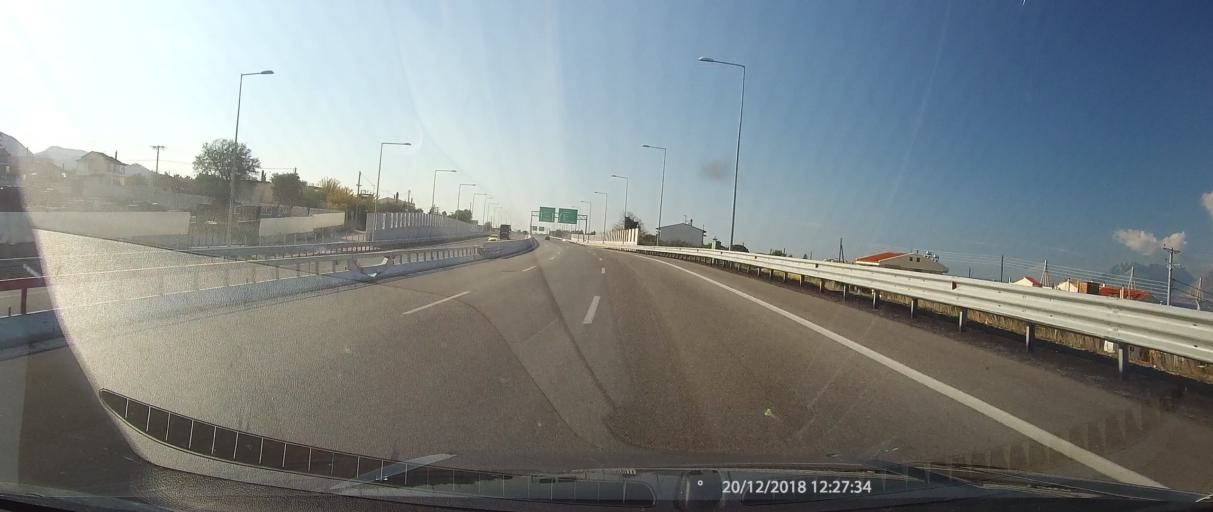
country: GR
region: West Greece
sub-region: Nomos Achaias
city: Rio
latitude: 38.3100
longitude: 21.8129
